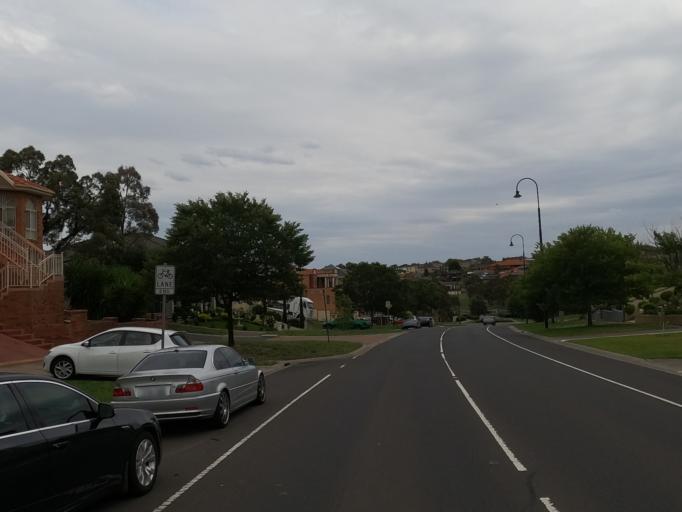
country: AU
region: Victoria
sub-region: Hume
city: Meadow Heights
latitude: -37.6434
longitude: 144.9071
